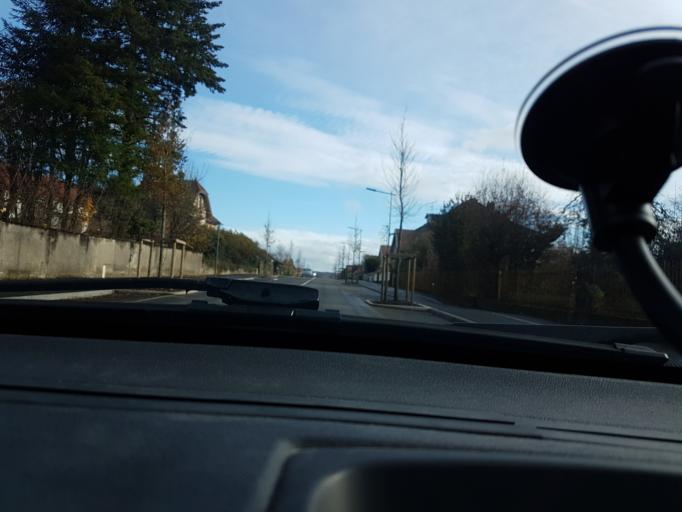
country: FR
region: Franche-Comte
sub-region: Territoire de Belfort
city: Bavilliers
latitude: 47.6233
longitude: 6.8414
